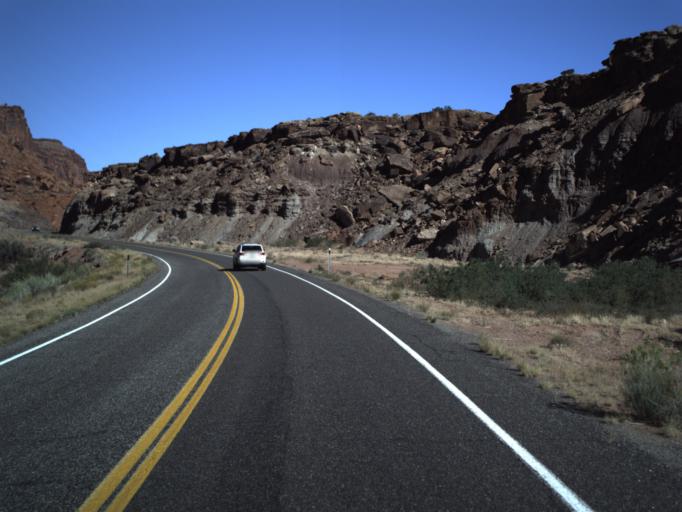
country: US
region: Utah
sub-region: San Juan County
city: Blanding
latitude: 37.9218
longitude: -110.4631
